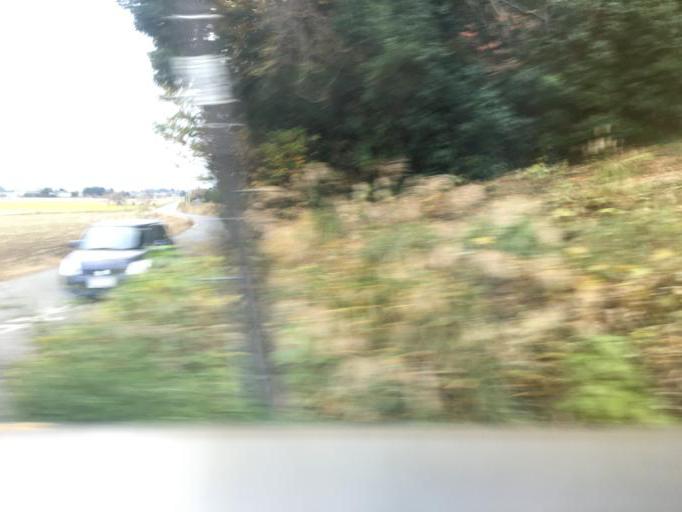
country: JP
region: Tochigi
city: Tochigi
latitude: 36.3379
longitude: 139.6796
